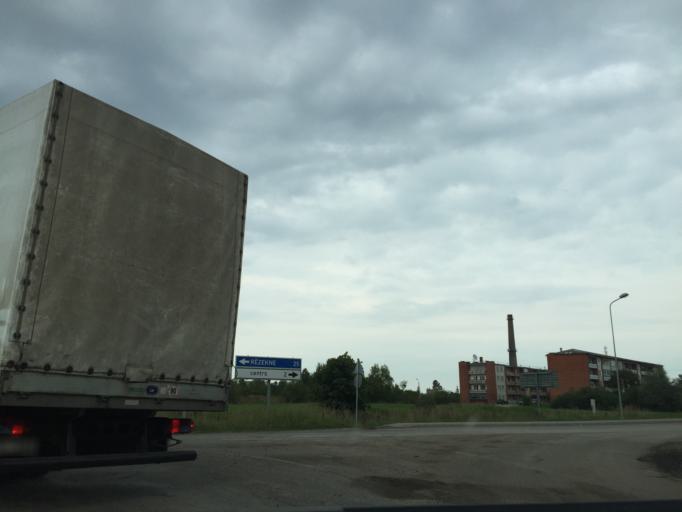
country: LV
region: Ludzas Rajons
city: Ludza
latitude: 56.5376
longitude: 27.6983
